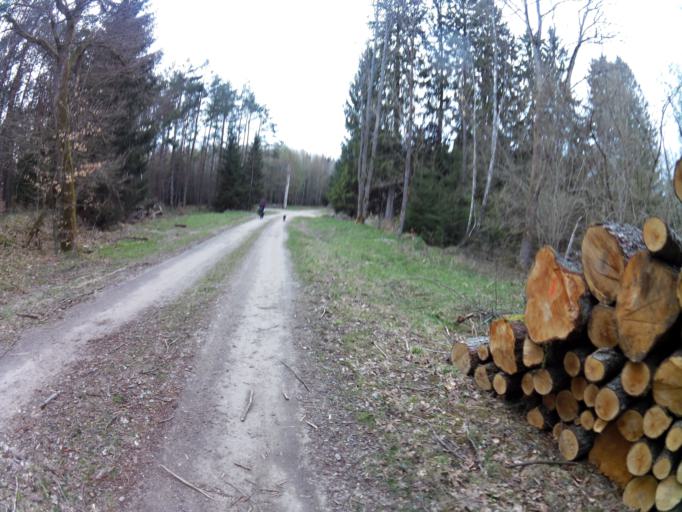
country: PL
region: West Pomeranian Voivodeship
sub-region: Powiat szczecinecki
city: Bialy Bor
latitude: 53.8868
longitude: 16.7184
